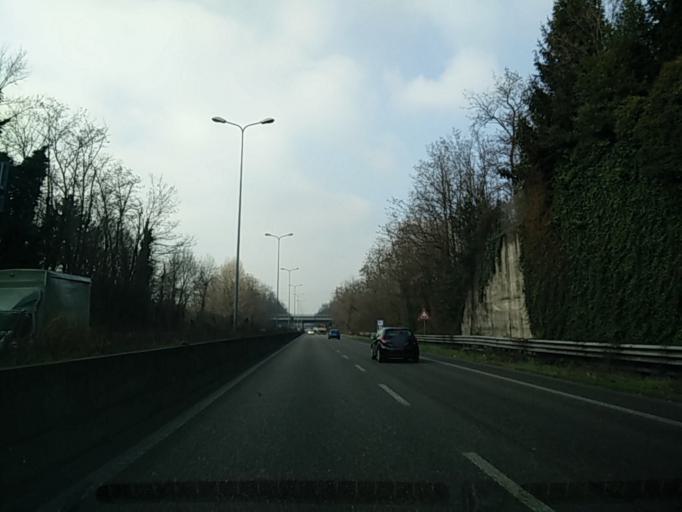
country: IT
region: Lombardy
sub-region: Provincia di Monza e Brianza
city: Varedo
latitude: 45.6001
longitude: 9.1708
